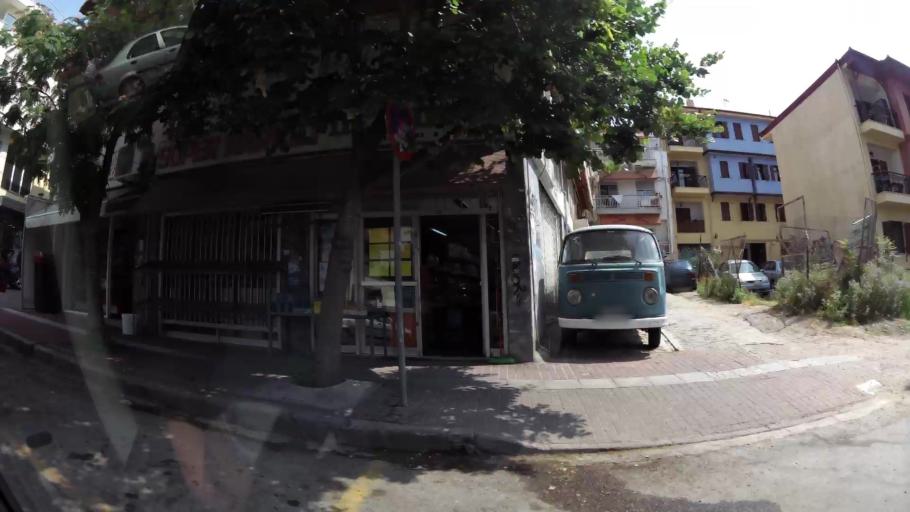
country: GR
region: Central Macedonia
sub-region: Nomos Thessalonikis
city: Sykies
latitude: 40.6406
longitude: 22.9501
